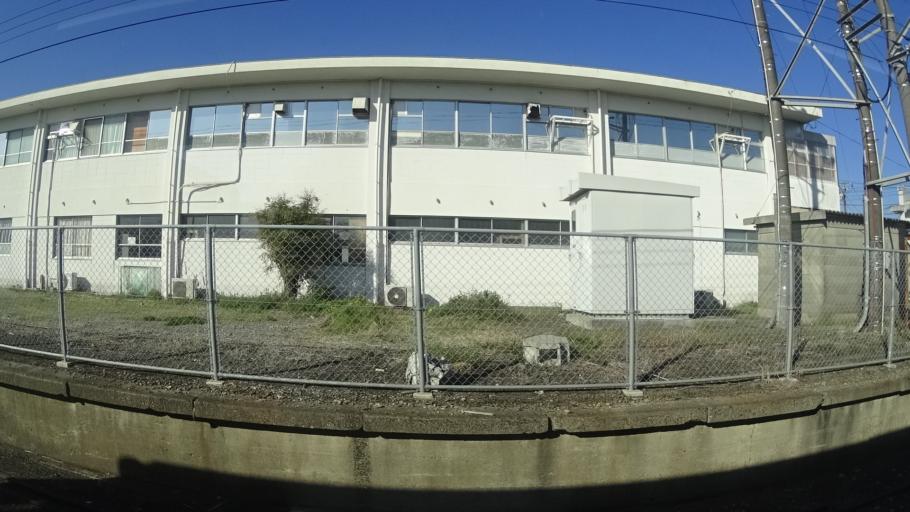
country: JP
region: Fukushima
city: Namie
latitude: 37.6365
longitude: 140.9726
